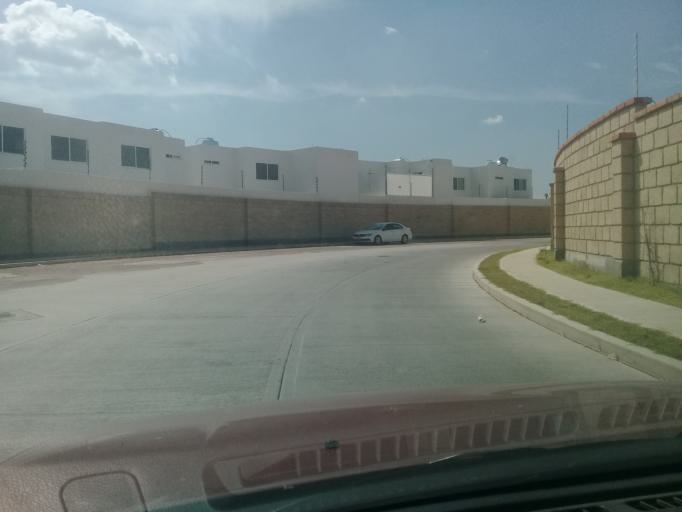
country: MX
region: Aguascalientes
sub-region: Aguascalientes
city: San Sebastian [Fraccionamiento]
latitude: 21.8329
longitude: -102.3129
